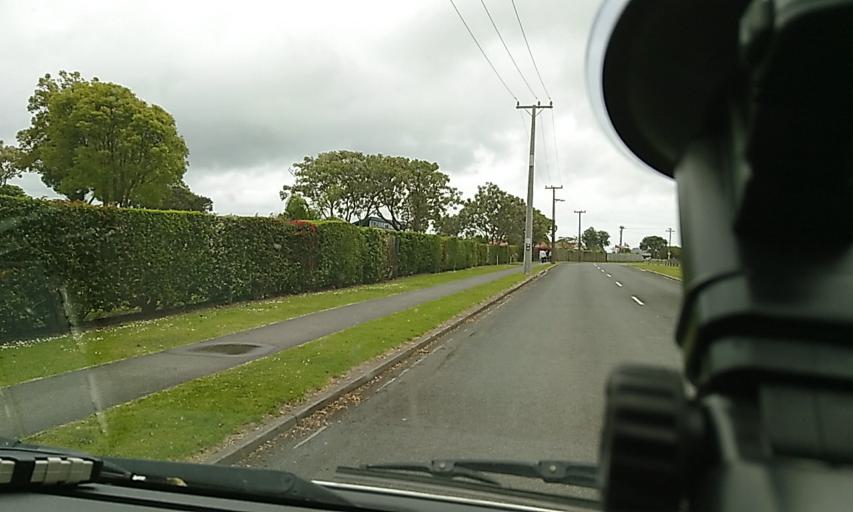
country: NZ
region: Northland
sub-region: Far North District
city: Paihia
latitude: -35.2762
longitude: 174.0779
